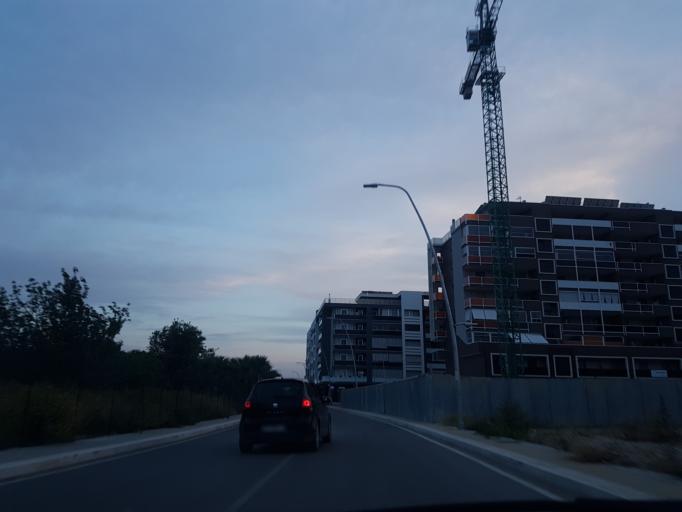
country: IT
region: Apulia
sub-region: Provincia di Barletta - Andria - Trani
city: Barletta
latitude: 41.3047
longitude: 16.2765
